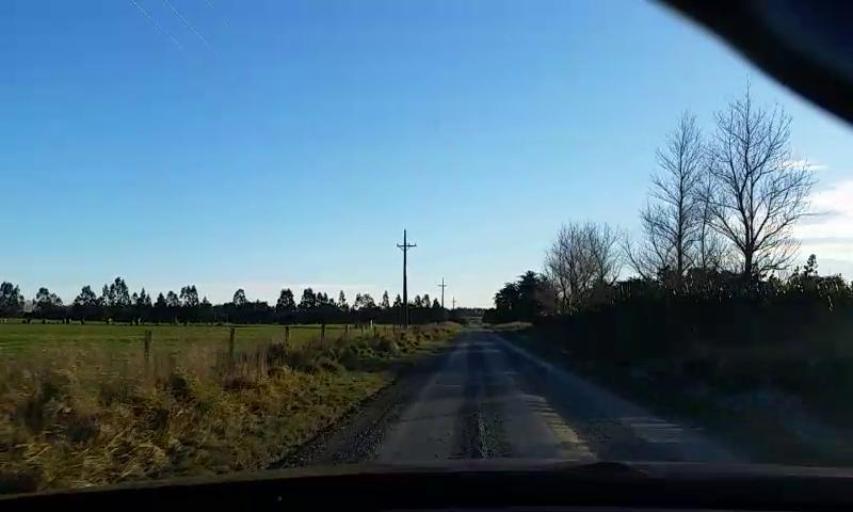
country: NZ
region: Southland
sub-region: Invercargill City
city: Invercargill
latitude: -46.2916
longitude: 168.4221
